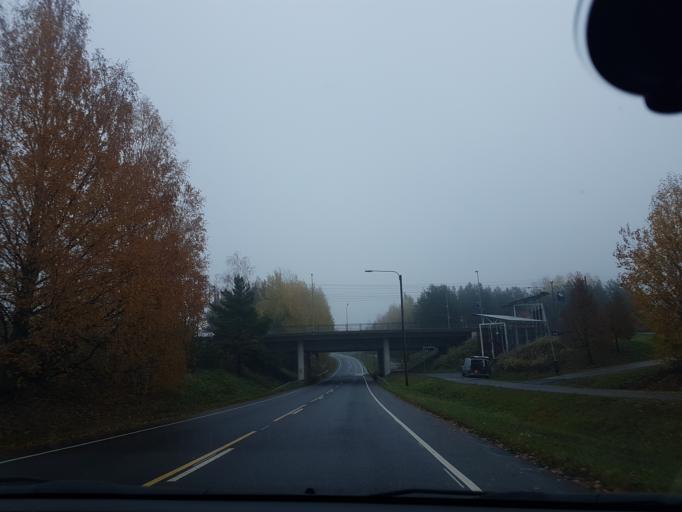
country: FI
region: Uusimaa
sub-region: Helsinki
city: Jaervenpaeae
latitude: 60.4557
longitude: 25.1002
